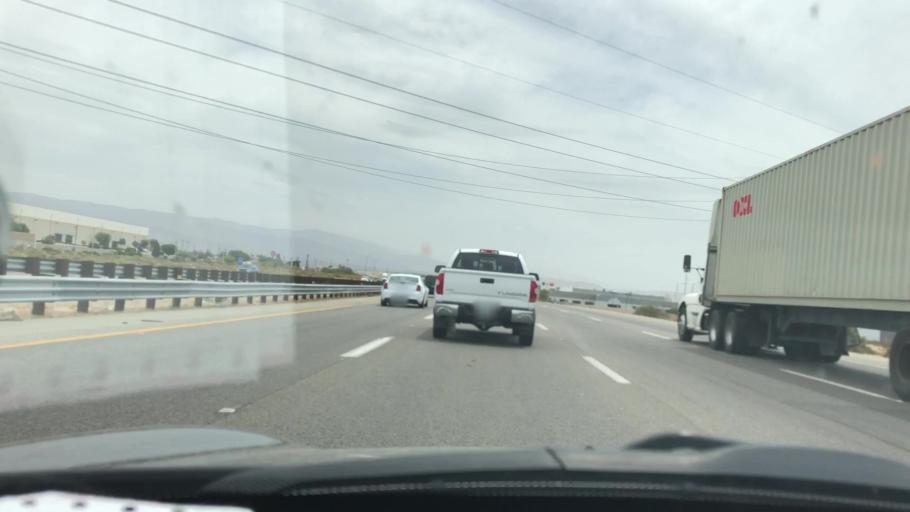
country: US
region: California
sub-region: Riverside County
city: Garnet
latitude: 33.9048
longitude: -116.5561
